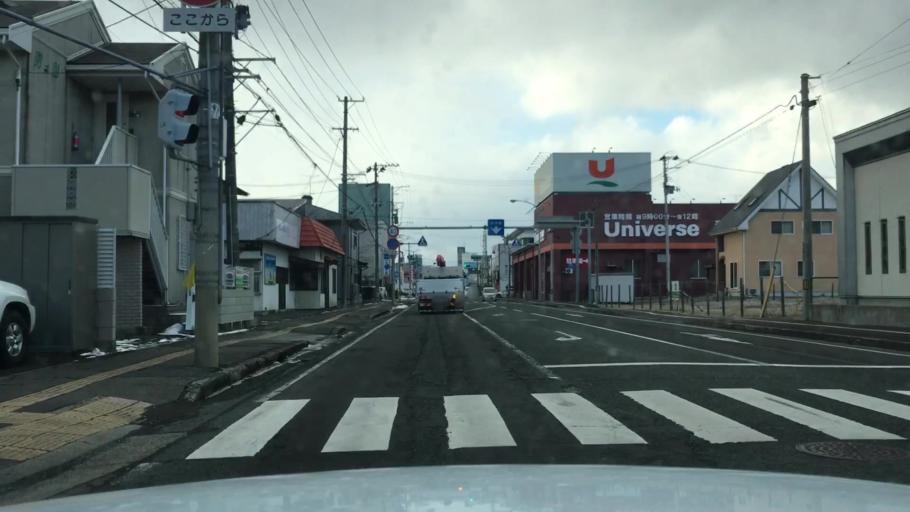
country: JP
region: Iwate
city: Morioka-shi
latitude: 39.6915
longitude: 141.1728
